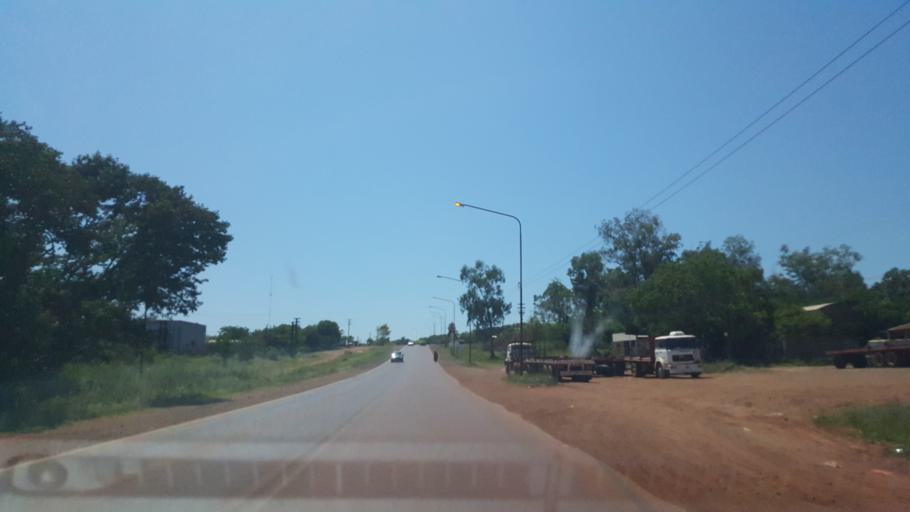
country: AR
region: Corrientes
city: Santo Tome
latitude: -28.5498
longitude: -56.0749
